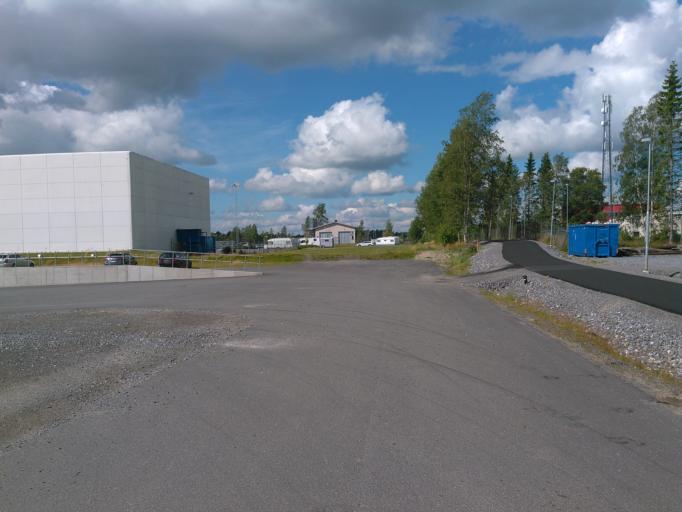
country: SE
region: Vaesterbotten
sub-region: Umea Kommun
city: Ersmark
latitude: 63.8499
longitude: 20.3201
